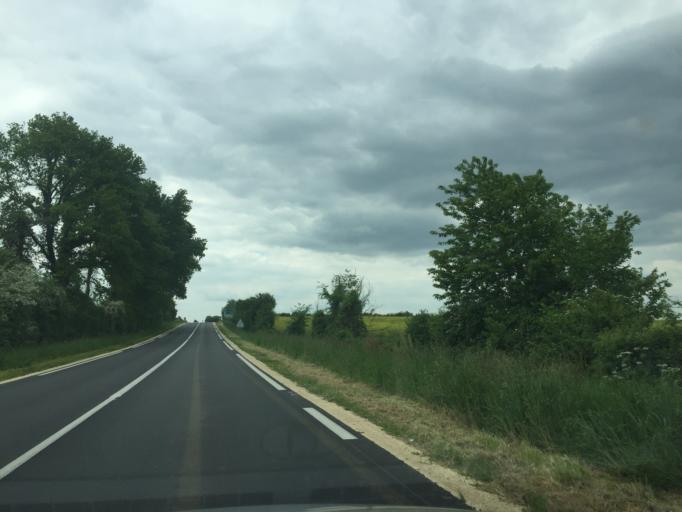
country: FR
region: Poitou-Charentes
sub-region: Departement de la Vienne
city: Lusignan
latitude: 46.4619
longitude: 0.1531
